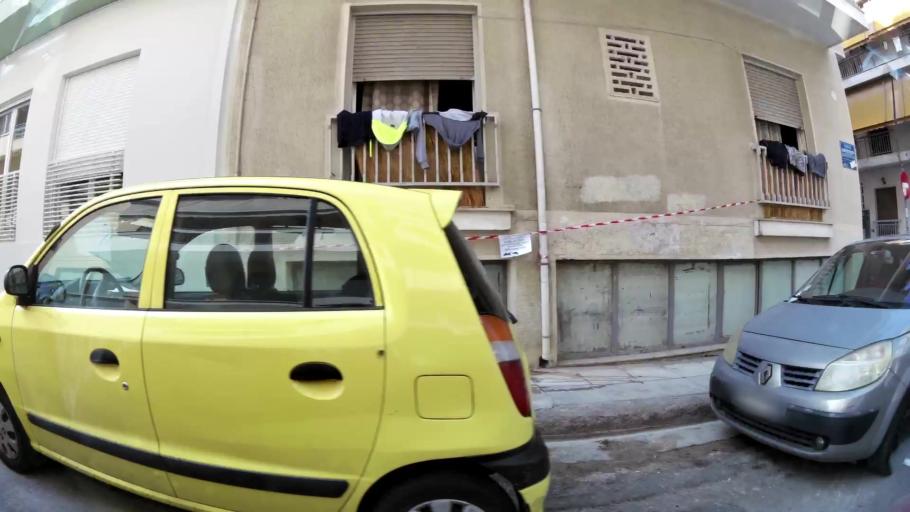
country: GR
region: Attica
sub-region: Nomarchia Athinas
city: Dhafni
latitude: 37.9623
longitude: 23.7317
